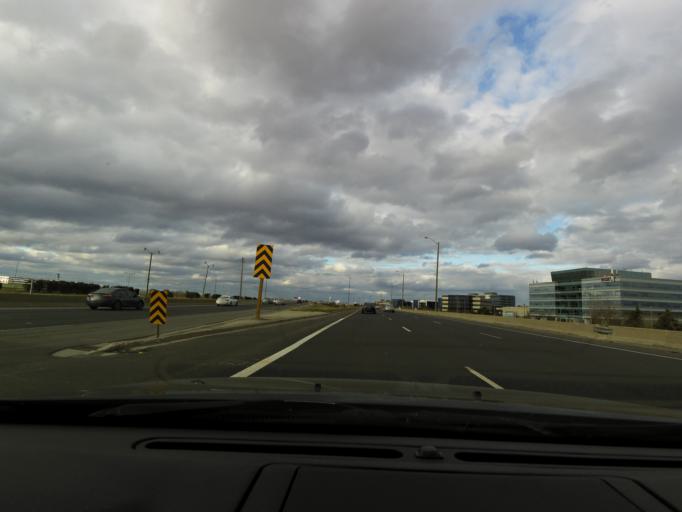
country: CA
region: Ontario
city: Etobicoke
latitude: 43.6562
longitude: -79.6176
